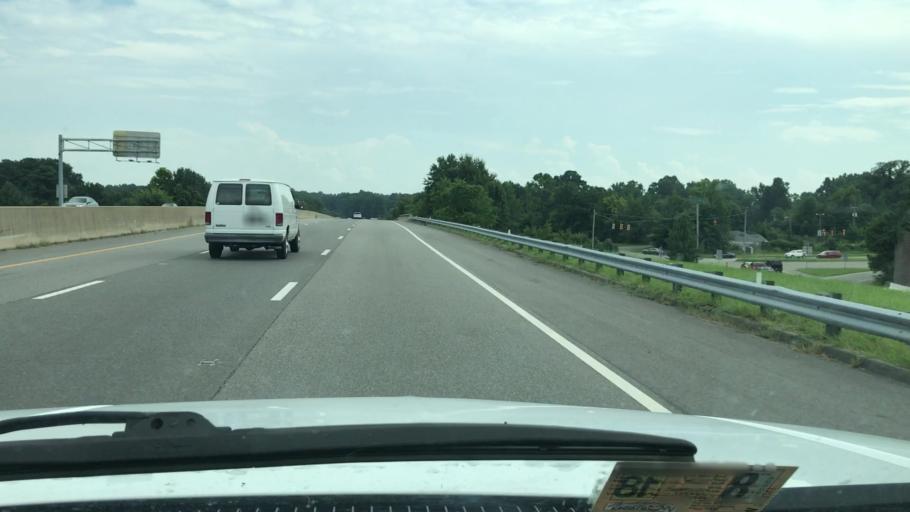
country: US
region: Virginia
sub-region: Chesterfield County
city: Bon Air
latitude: 37.4799
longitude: -77.5159
